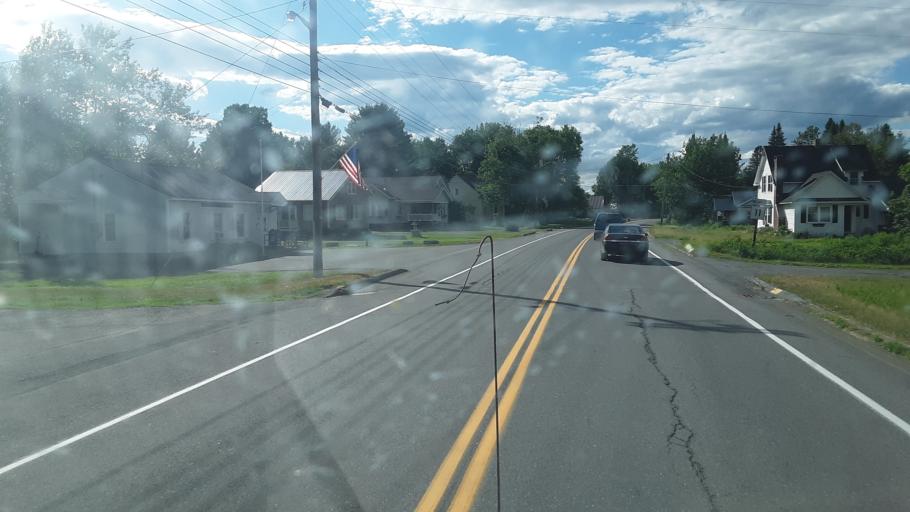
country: US
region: Maine
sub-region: Penobscot County
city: Patten
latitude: 45.9002
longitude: -68.4305
